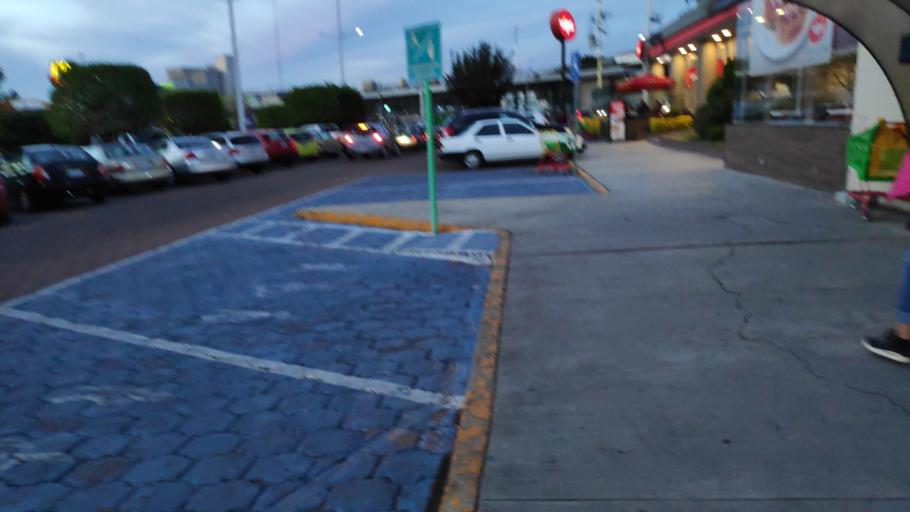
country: MX
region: Queretaro
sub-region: Queretaro
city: Santiago de Queretaro
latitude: 20.5858
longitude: -100.3825
